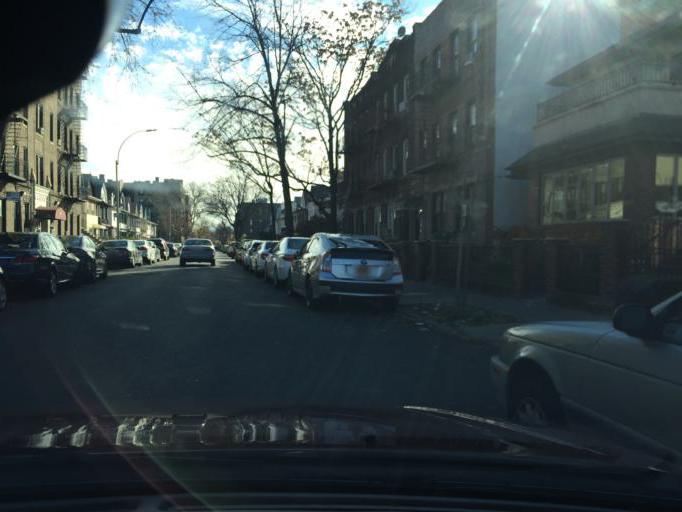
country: US
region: New York
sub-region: Kings County
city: Brooklyn
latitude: 40.6247
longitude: -73.9623
